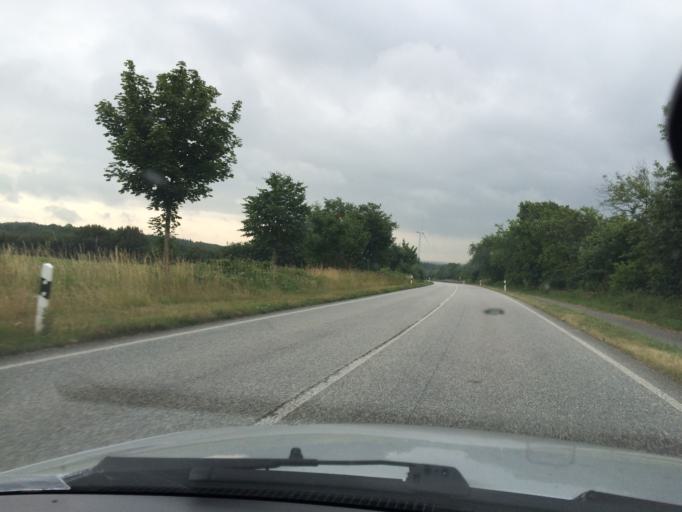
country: DE
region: Schleswig-Holstein
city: Tarp
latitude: 54.6575
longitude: 9.4414
